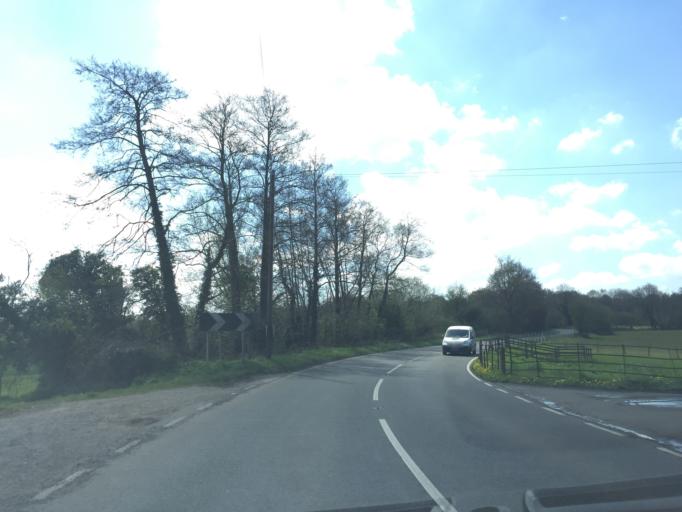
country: GB
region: England
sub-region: East Sussex
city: Crowborough
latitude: 51.1094
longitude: 0.1132
